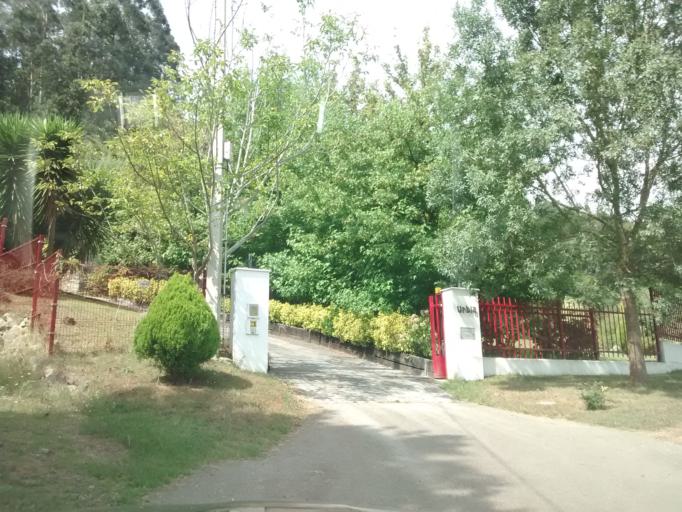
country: ES
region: Cantabria
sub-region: Provincia de Cantabria
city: Miengo
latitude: 43.4112
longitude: -3.9611
